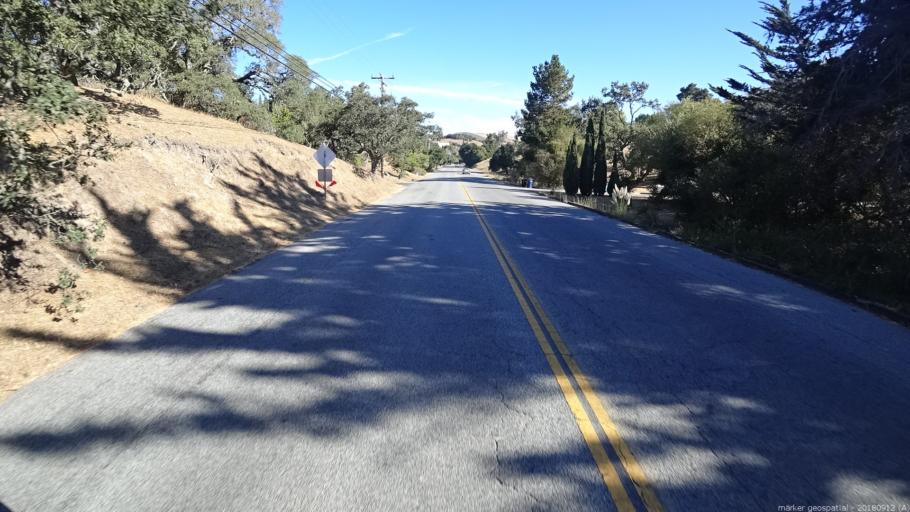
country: US
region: California
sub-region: Monterey County
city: Carmel Valley Village
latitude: 36.5693
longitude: -121.7308
